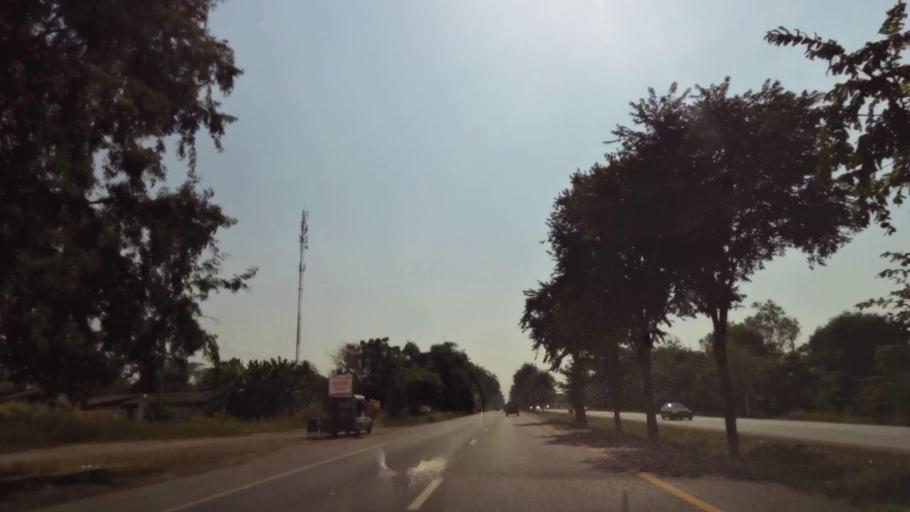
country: TH
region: Phichit
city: Bueng Na Rang
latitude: 16.0956
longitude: 100.1254
